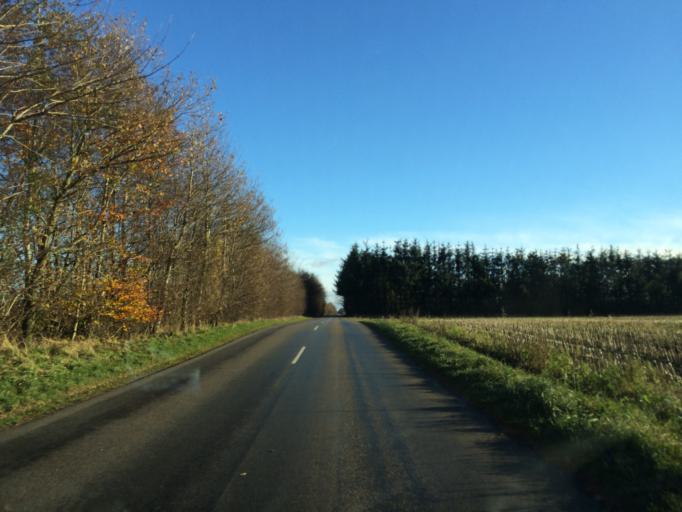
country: DK
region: Central Jutland
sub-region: Herning Kommune
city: Kibaek
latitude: 56.0537
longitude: 8.7874
